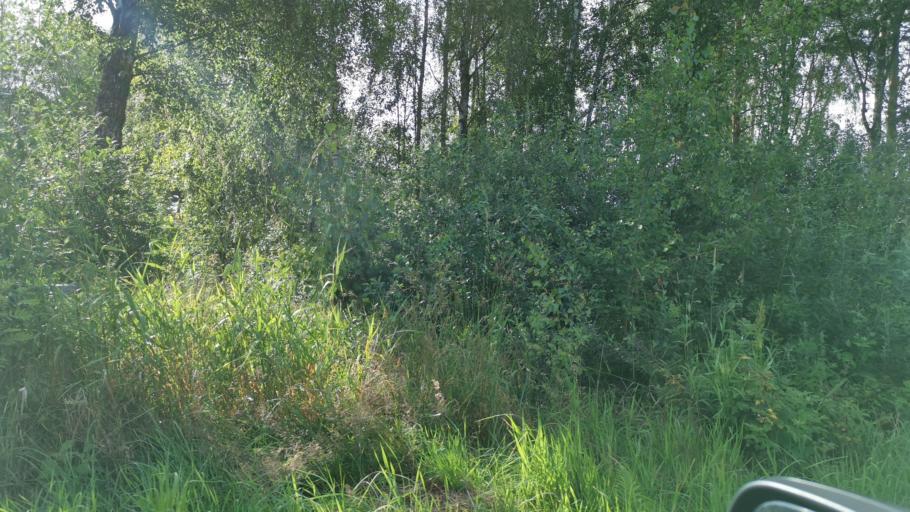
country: SE
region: Vaestra Goetaland
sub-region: Tjorns Kommun
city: Myggenas
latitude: 58.1034
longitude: 11.6382
